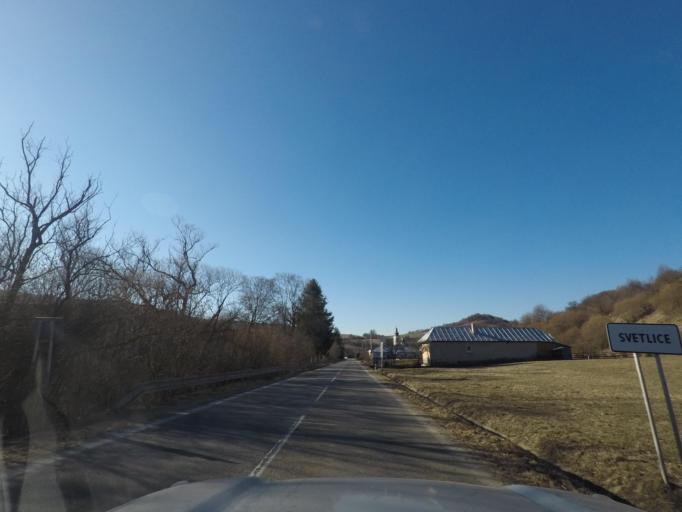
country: PL
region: Subcarpathian Voivodeship
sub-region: Powiat sanocki
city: Komancza
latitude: 49.1618
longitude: 22.0440
